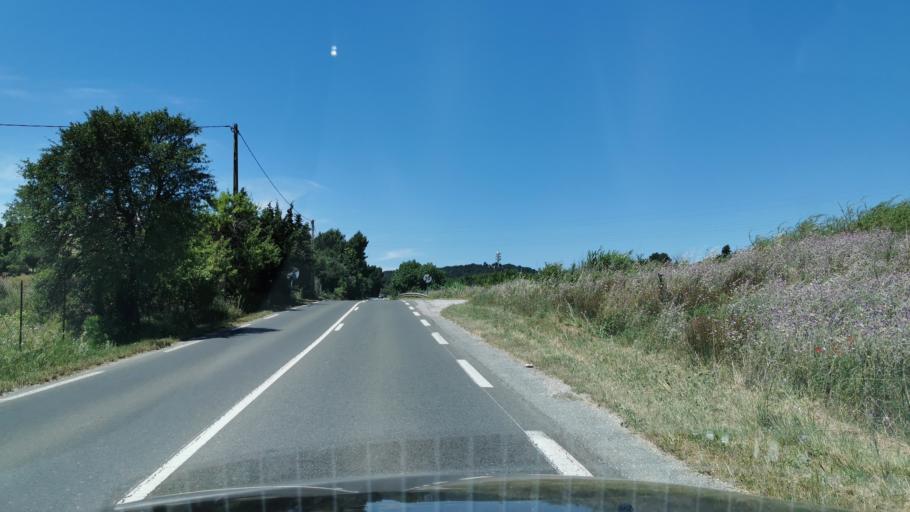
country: FR
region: Languedoc-Roussillon
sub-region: Departement de l'Aude
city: Moussan
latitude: 43.2009
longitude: 2.9684
